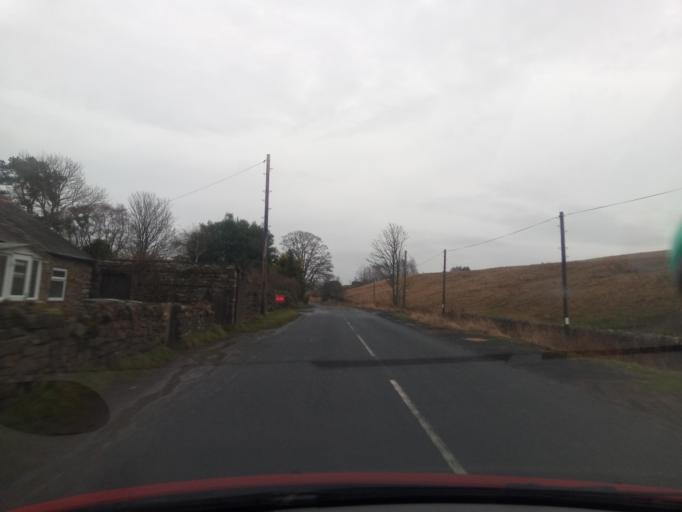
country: GB
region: England
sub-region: Northumberland
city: Rochester
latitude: 55.1661
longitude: -2.3728
